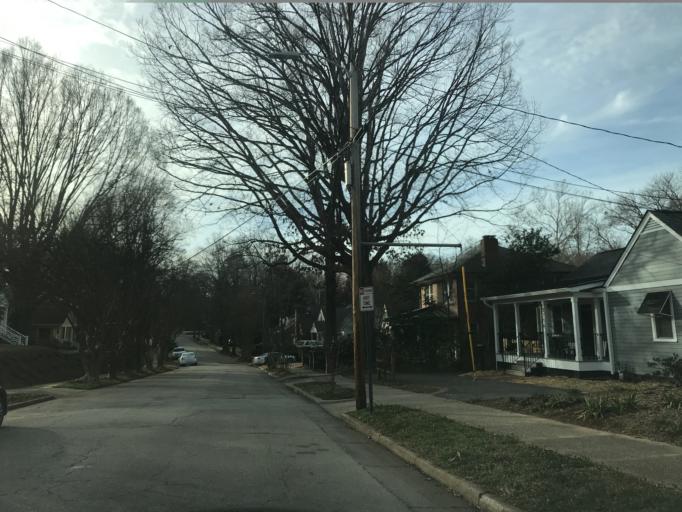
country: US
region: North Carolina
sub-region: Wake County
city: West Raleigh
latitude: 35.7920
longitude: -78.6711
